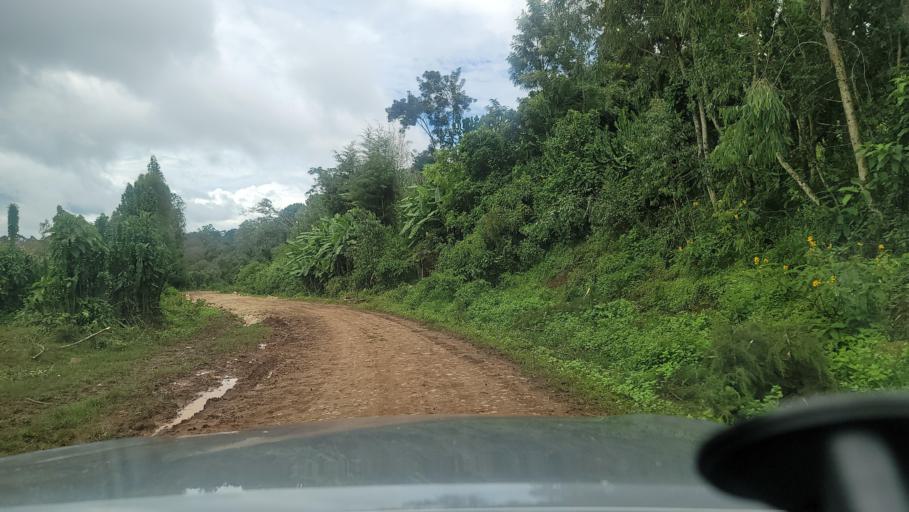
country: ET
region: Southern Nations, Nationalities, and People's Region
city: Bonga
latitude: 7.6332
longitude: 36.2211
